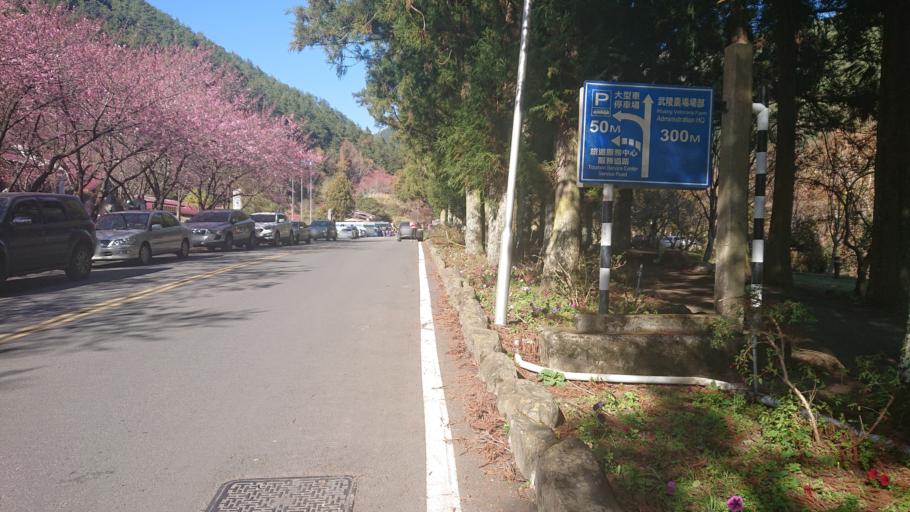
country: TW
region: Taiwan
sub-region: Hualien
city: Hualian
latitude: 24.3522
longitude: 121.3098
